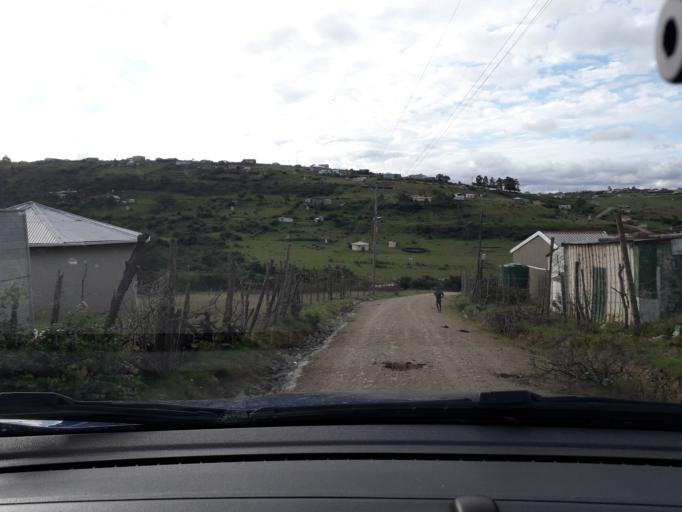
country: ZA
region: Eastern Cape
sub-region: Buffalo City Metropolitan Municipality
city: East London
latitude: -32.8039
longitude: 27.9608
